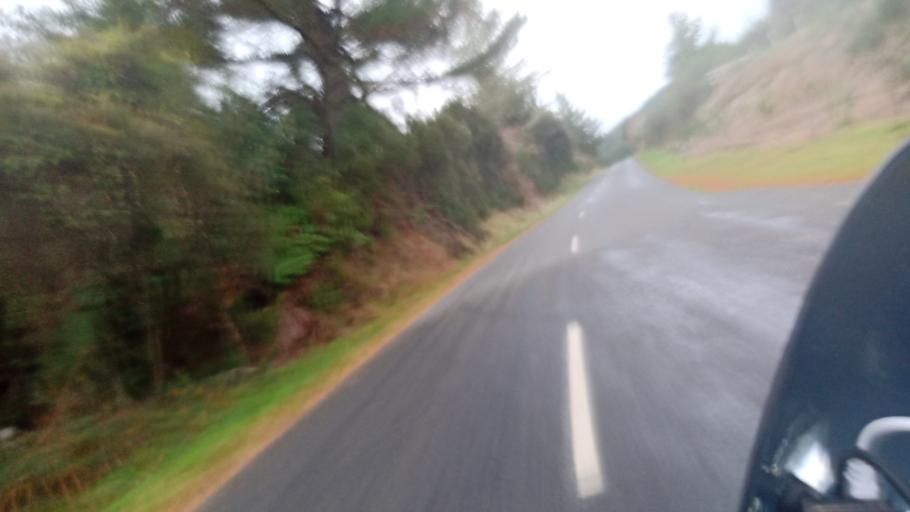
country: NZ
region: Bay of Plenty
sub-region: Whakatane District
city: Murupara
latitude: -38.6255
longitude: 176.7364
